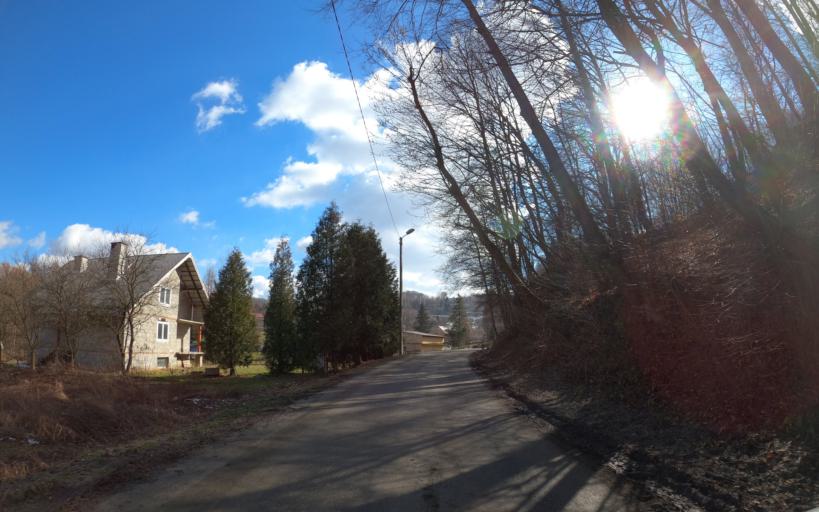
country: PL
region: Subcarpathian Voivodeship
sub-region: Powiat debicki
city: Debica
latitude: 50.0339
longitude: 21.4371
